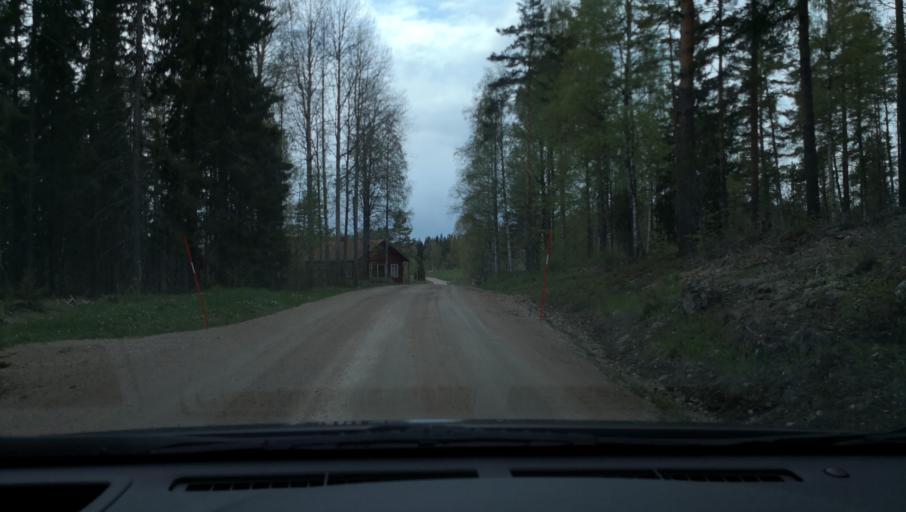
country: SE
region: Vaestmanland
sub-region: Fagersta Kommun
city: Fagersta
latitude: 60.1205
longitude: 15.7481
